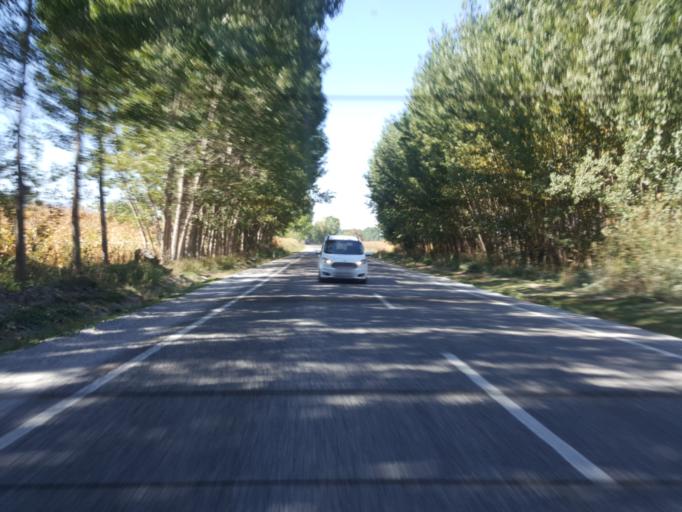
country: TR
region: Tokat
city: Pazar
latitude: 40.2697
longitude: 36.2287
